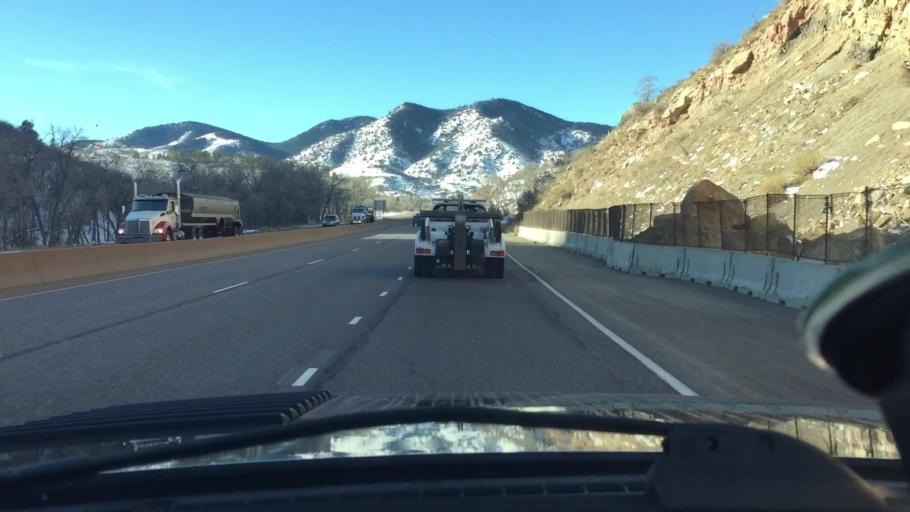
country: US
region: Colorado
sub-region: Jefferson County
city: Indian Hills
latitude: 39.6341
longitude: -105.1712
